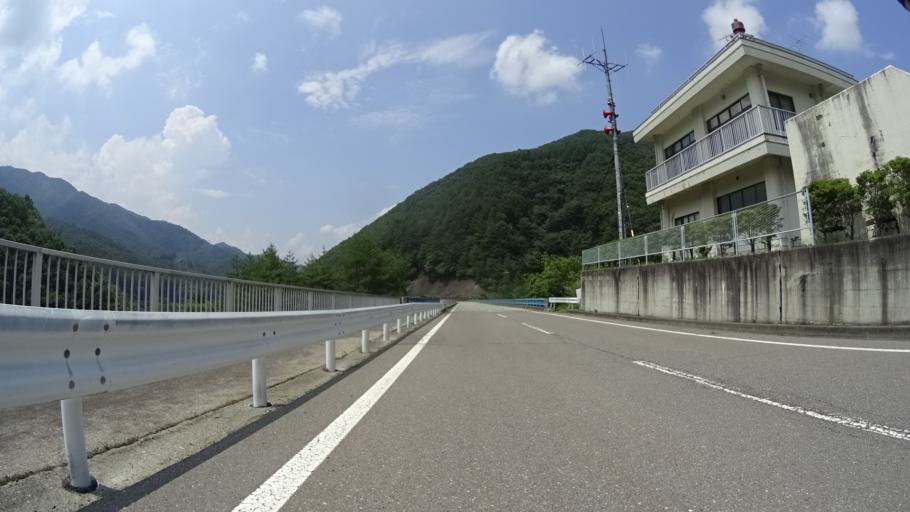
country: JP
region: Nagano
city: Saku
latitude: 36.1249
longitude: 138.5945
